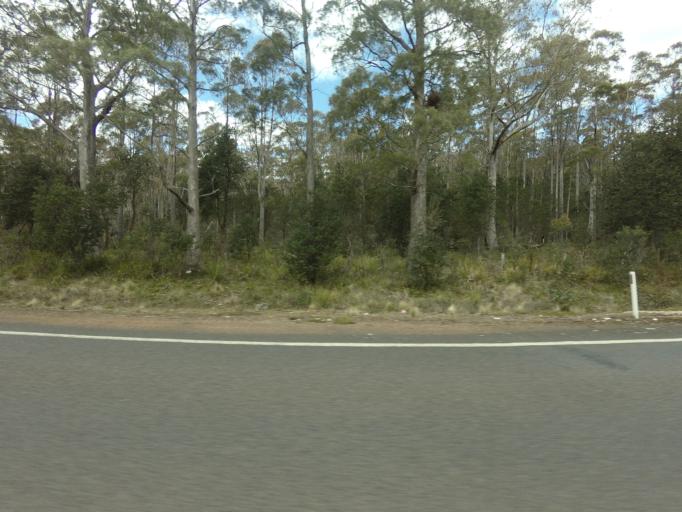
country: AU
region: Tasmania
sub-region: Northern Midlands
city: Evandale
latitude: -42.0087
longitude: 147.7236
